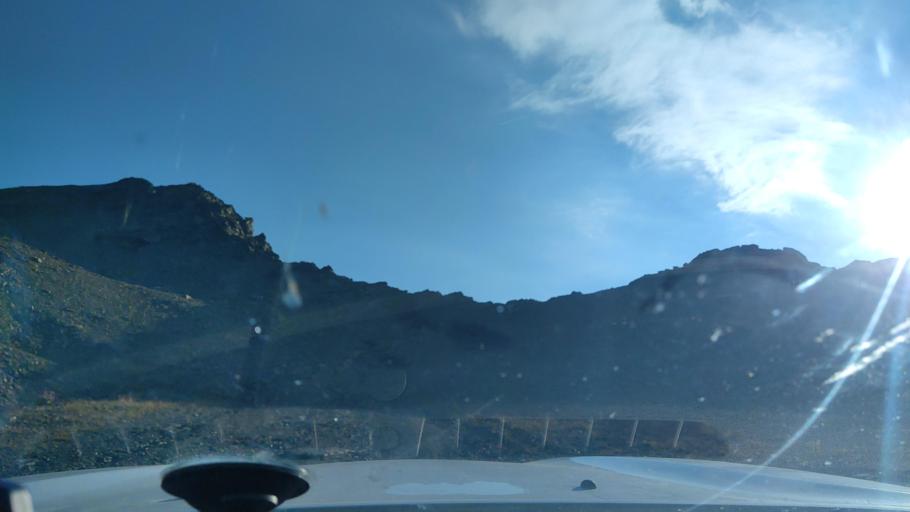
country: FR
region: Rhone-Alpes
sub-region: Departement de la Savoie
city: Val Thorens
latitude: 45.2601
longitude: 6.5745
